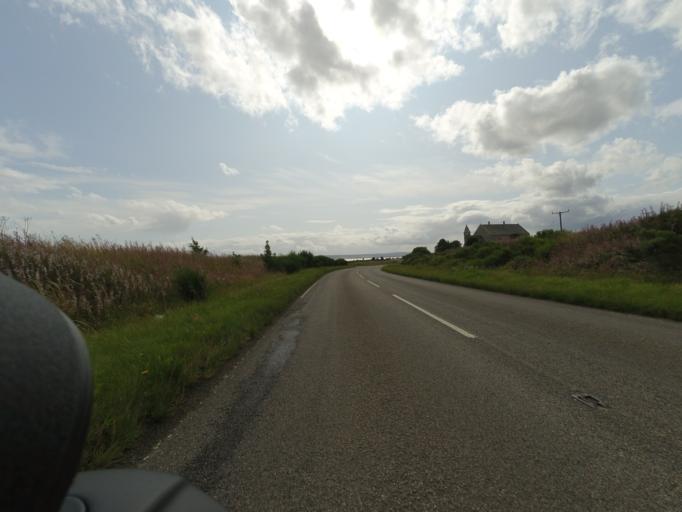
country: GB
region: Scotland
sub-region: Highland
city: Tain
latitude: 57.7321
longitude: -4.0861
